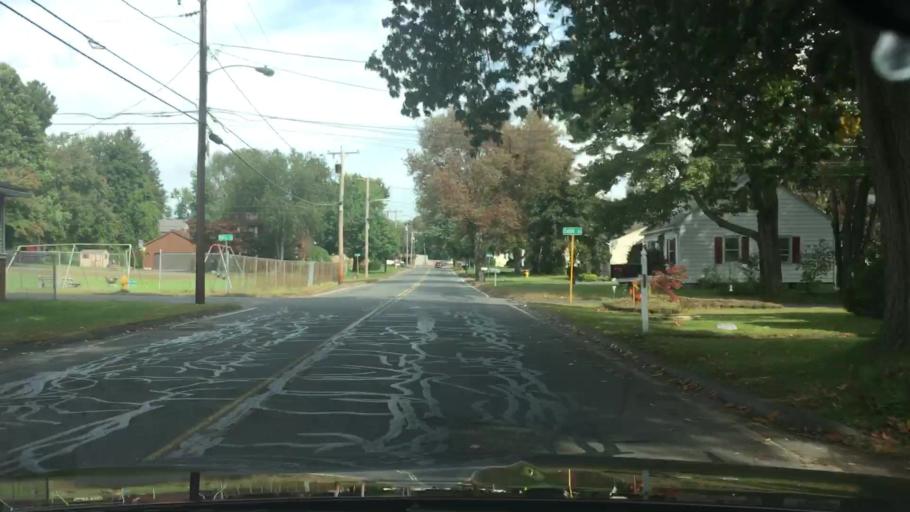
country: US
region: Massachusetts
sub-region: Hampden County
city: East Longmeadow
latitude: 42.0767
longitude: -72.5322
